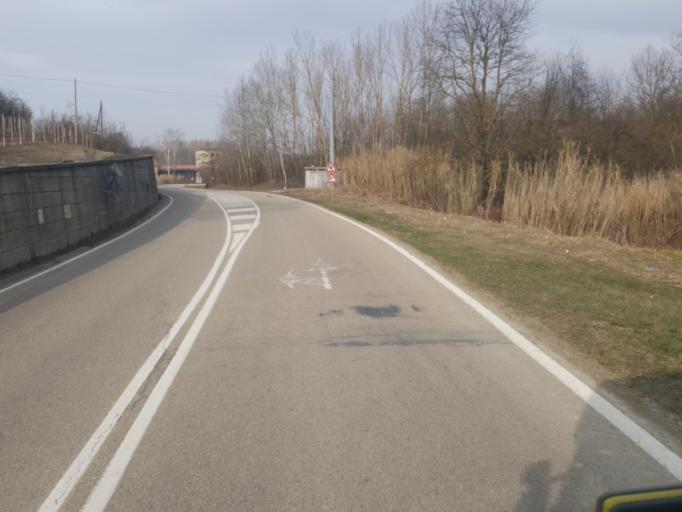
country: IT
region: Piedmont
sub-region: Provincia di Asti
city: Bruno
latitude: 44.7937
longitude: 8.4252
